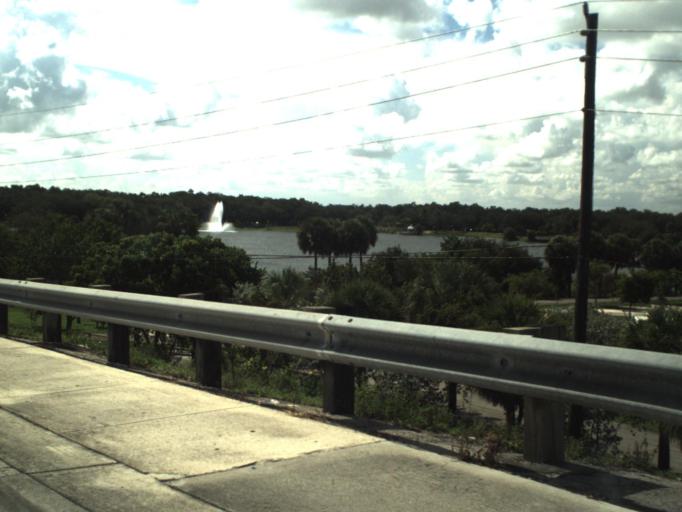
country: US
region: Florida
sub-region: Broward County
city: Hollywood
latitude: 26.0336
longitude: -80.1689
